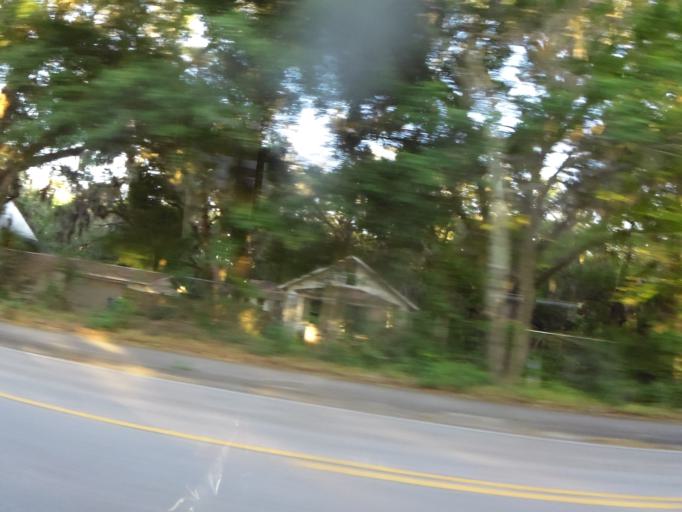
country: US
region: Florida
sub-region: Duval County
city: Jacksonville
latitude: 30.3338
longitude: -81.5829
